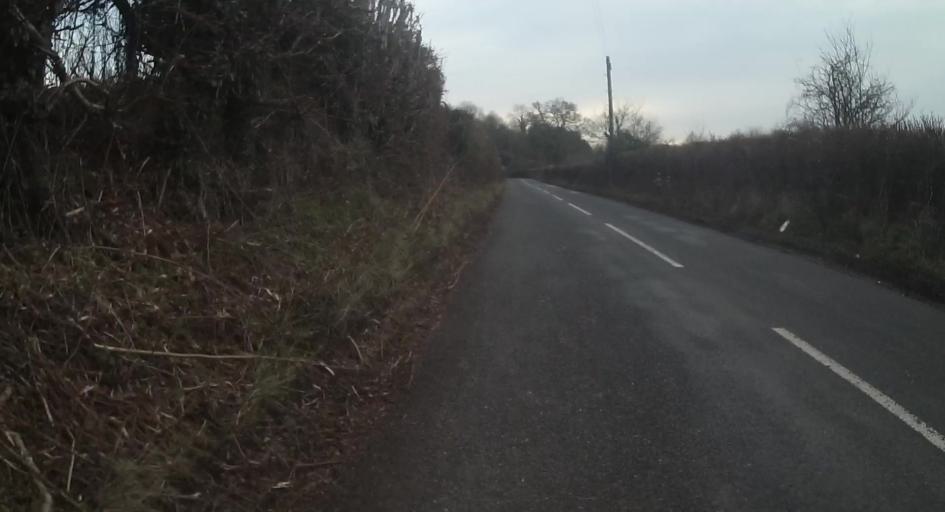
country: GB
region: England
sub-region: Hampshire
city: Highclere
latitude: 51.2339
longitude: -1.3817
